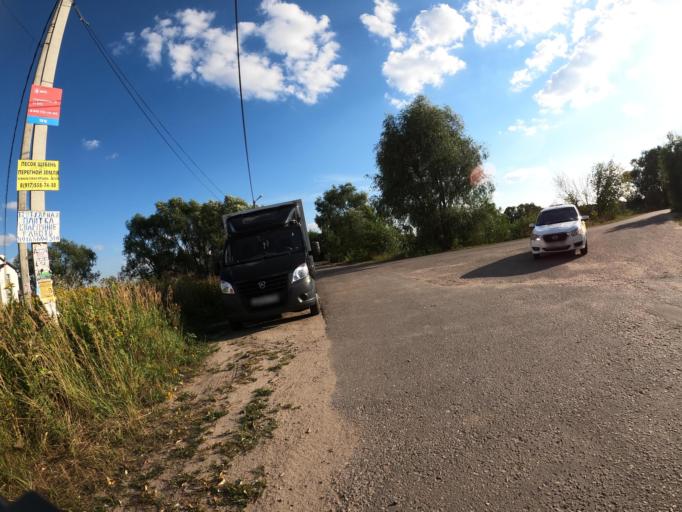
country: RU
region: Moskovskaya
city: Raduzhnyy
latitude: 55.1529
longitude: 38.7378
